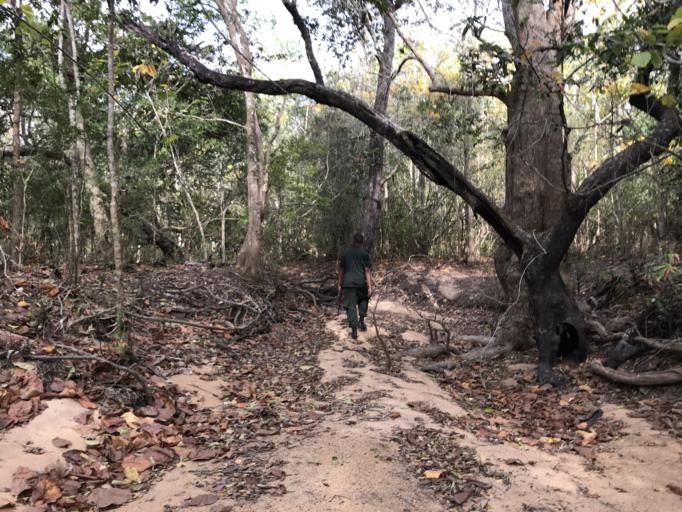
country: LK
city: Padaviya Divisional Secretariat
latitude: 9.0837
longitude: 80.8022
